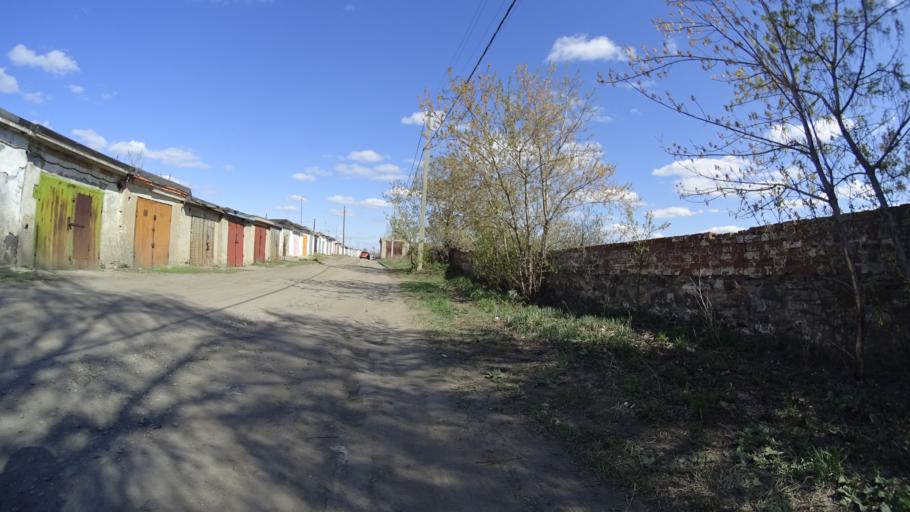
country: RU
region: Chelyabinsk
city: Troitsk
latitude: 54.0832
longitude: 61.5235
